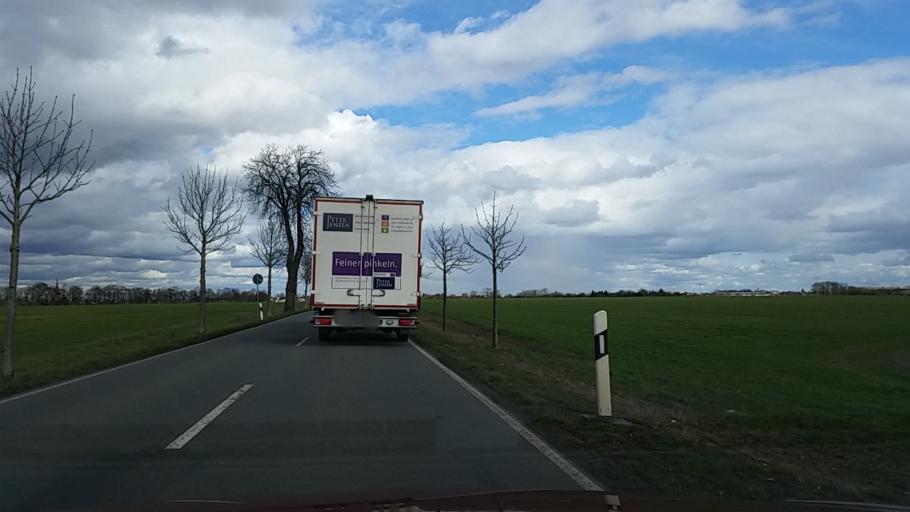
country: DE
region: Saxony-Anhalt
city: Salzwedel
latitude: 52.8307
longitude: 11.1415
